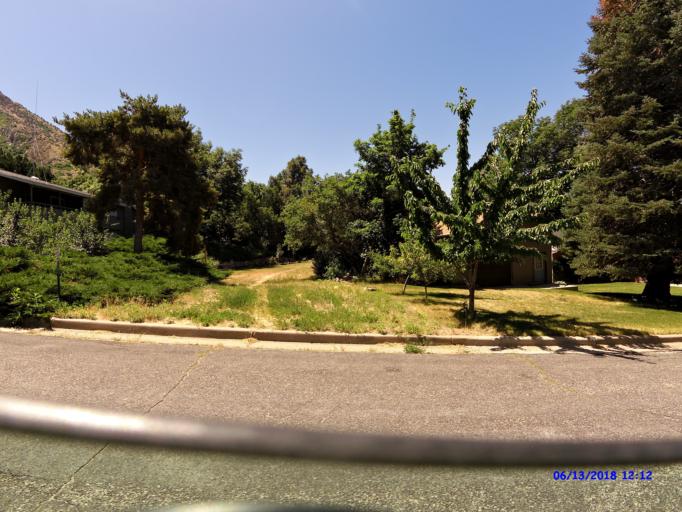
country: US
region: Utah
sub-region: Weber County
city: Ogden
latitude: 41.2149
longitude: -111.9323
